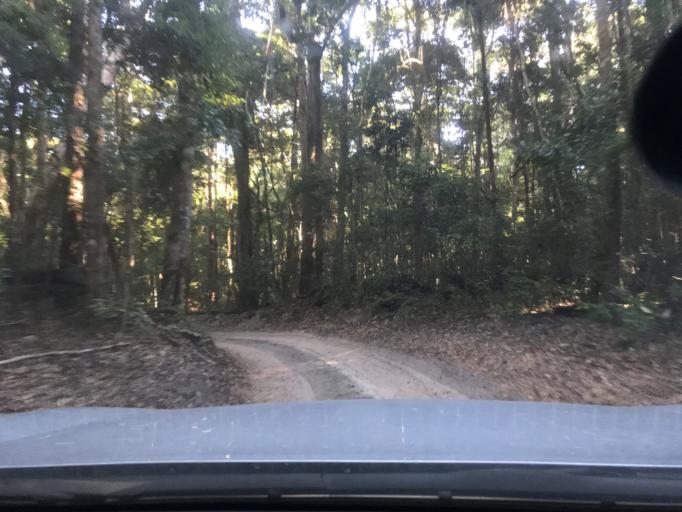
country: AU
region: Queensland
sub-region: Fraser Coast
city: Urangan
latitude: -25.3251
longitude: 153.1507
